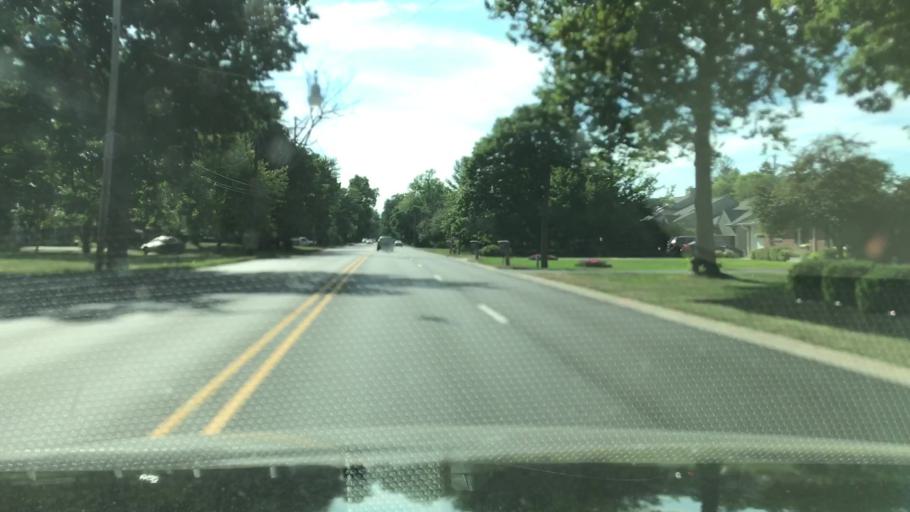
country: US
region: Michigan
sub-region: Kent County
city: East Grand Rapids
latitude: 42.9576
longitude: -85.5938
